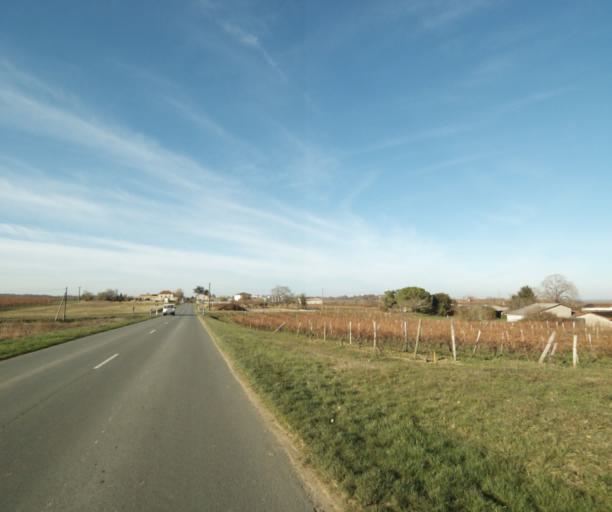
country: FR
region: Poitou-Charentes
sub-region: Departement de la Charente-Maritime
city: Burie
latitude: 45.7821
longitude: -0.4278
